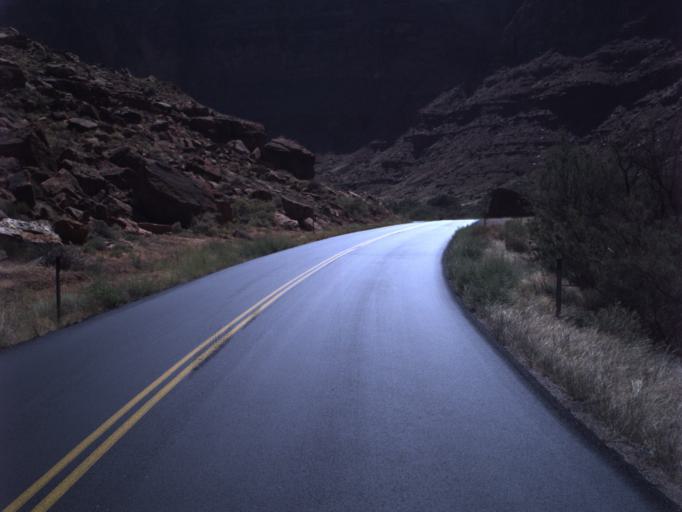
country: US
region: Utah
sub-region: Grand County
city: Moab
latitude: 38.6506
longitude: -109.5056
